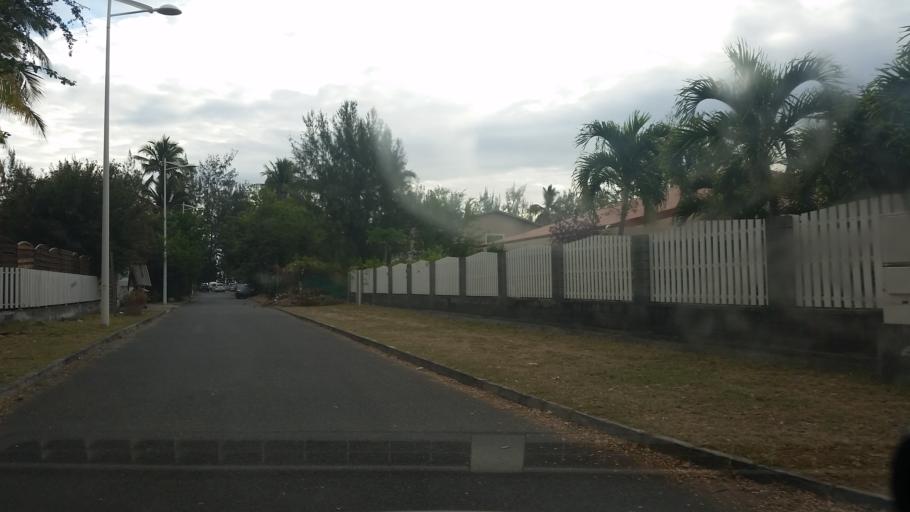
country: RE
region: Reunion
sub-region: Reunion
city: Trois-Bassins
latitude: -21.0790
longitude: 55.2243
